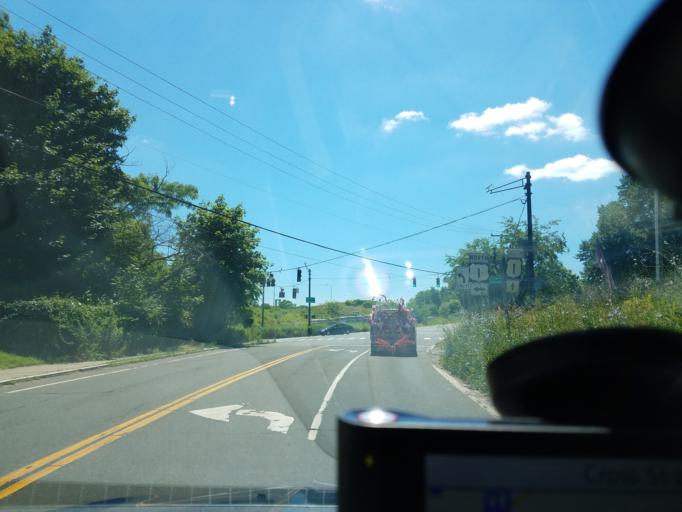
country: US
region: Connecticut
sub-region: Fairfield County
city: Norwalk
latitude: 41.1183
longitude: -73.4213
